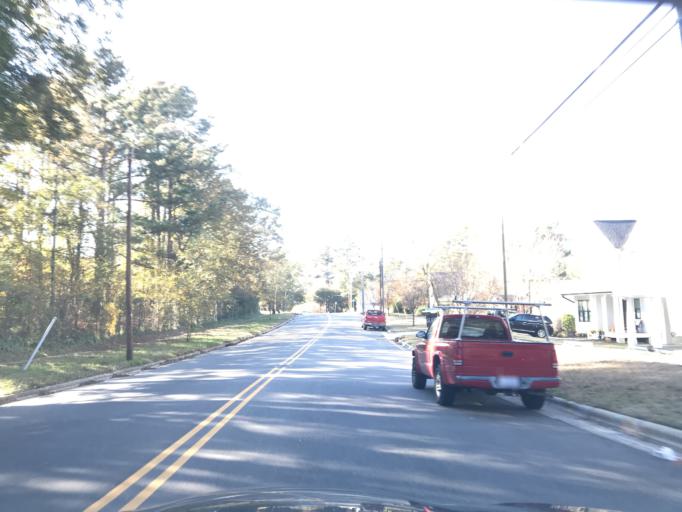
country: US
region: North Carolina
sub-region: Wake County
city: Raleigh
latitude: 35.7927
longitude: -78.6188
